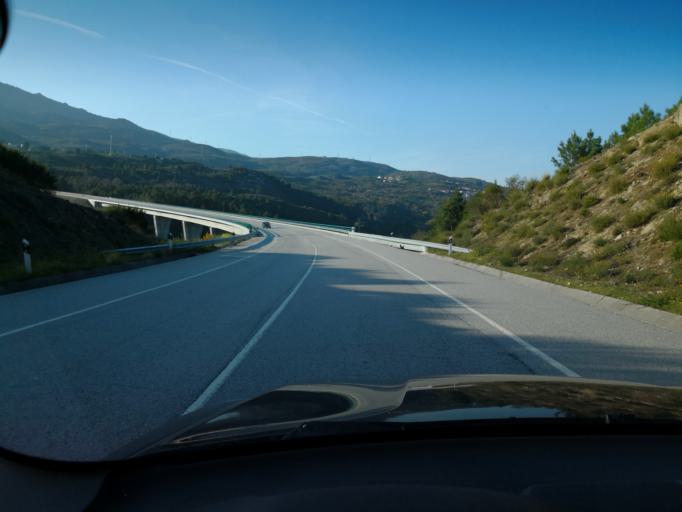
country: PT
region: Vila Real
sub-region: Vila Real
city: Vila Real
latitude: 41.3637
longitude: -7.7080
